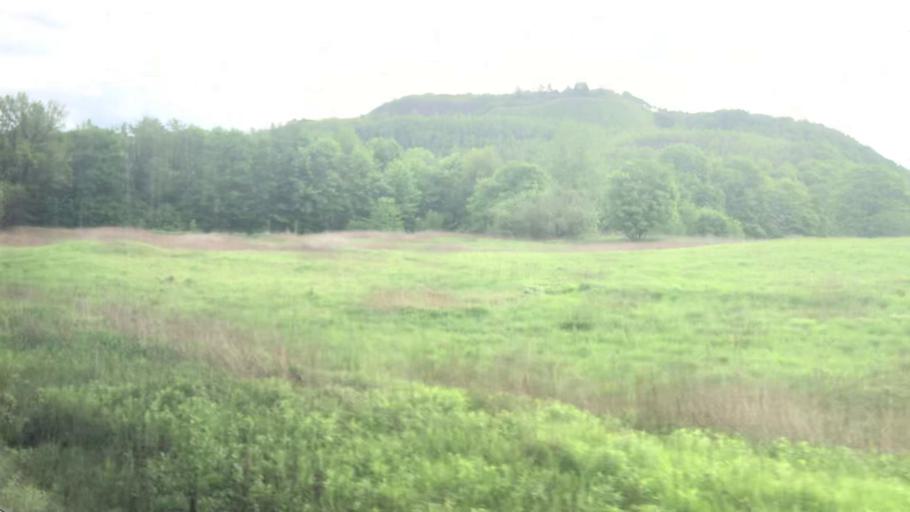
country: PL
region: Lower Silesian Voivodeship
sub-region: Powiat walbrzyski
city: Walbrzych
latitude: 50.7636
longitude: 16.2533
